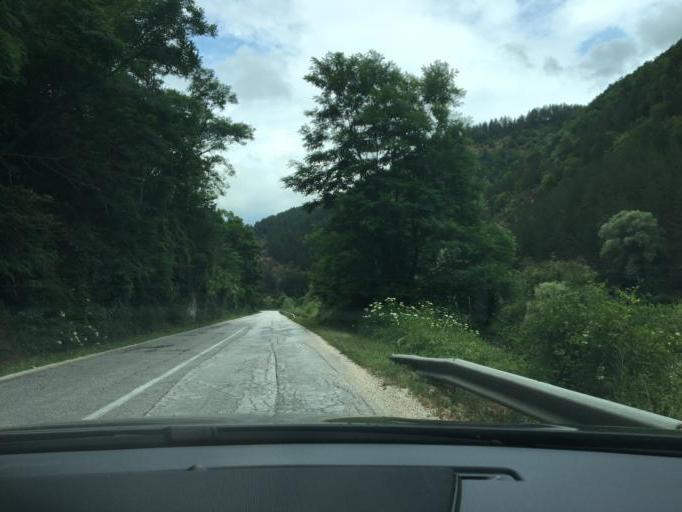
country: MK
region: Kriva Palanka
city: Kriva Palanka
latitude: 42.2274
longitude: 22.3831
